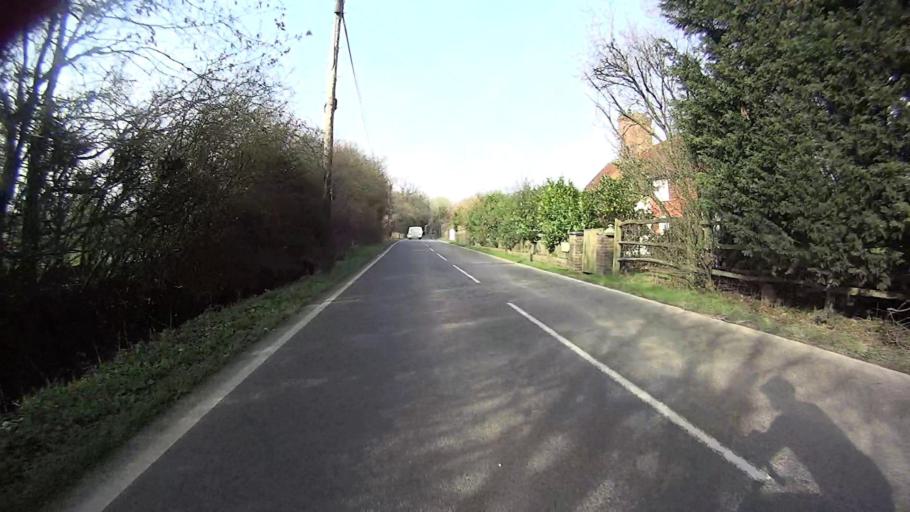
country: GB
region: England
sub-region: West Sussex
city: Copthorne
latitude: 51.1794
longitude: -0.0877
